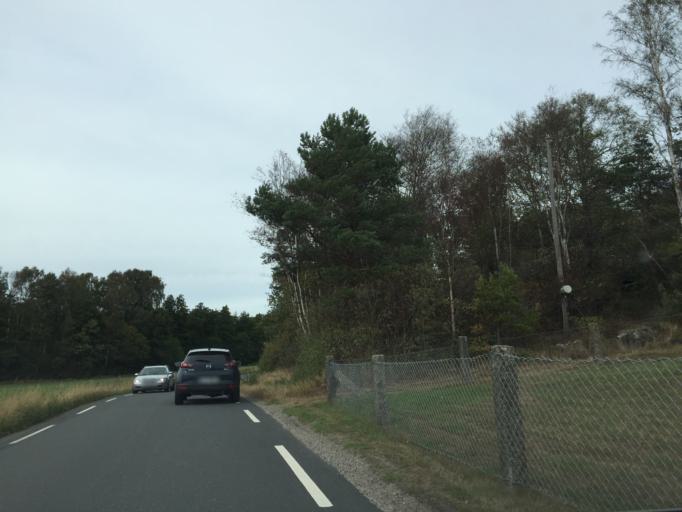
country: NO
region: Ostfold
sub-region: Hvaler
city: Skjaerhalden
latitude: 59.0384
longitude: 11.0279
